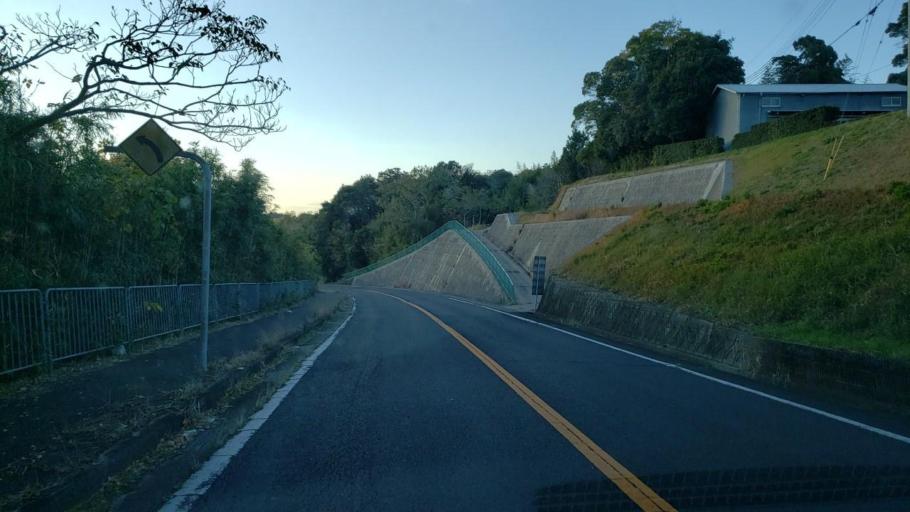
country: JP
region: Hyogo
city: Sumoto
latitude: 34.4401
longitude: 134.8829
